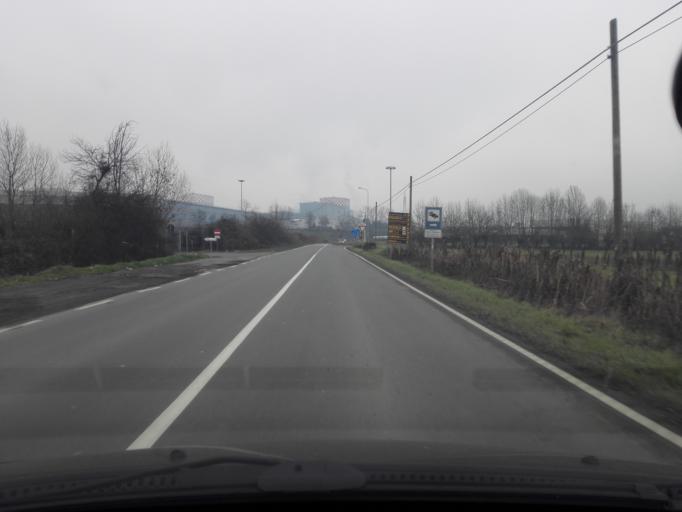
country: IT
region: Piedmont
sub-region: Provincia di Alessandria
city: Pasturana
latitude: 44.7809
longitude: 8.7532
